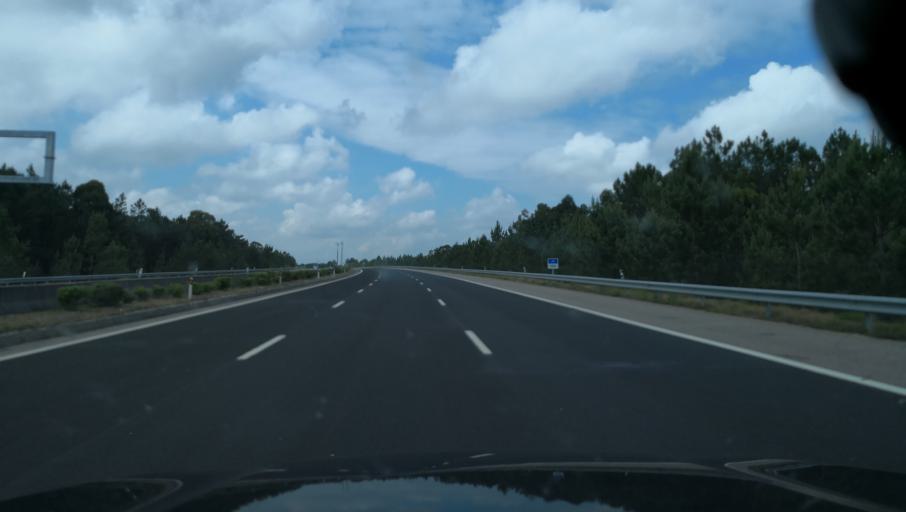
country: PT
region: Leiria
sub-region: Leiria
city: Maceira
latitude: 39.6936
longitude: -8.9294
